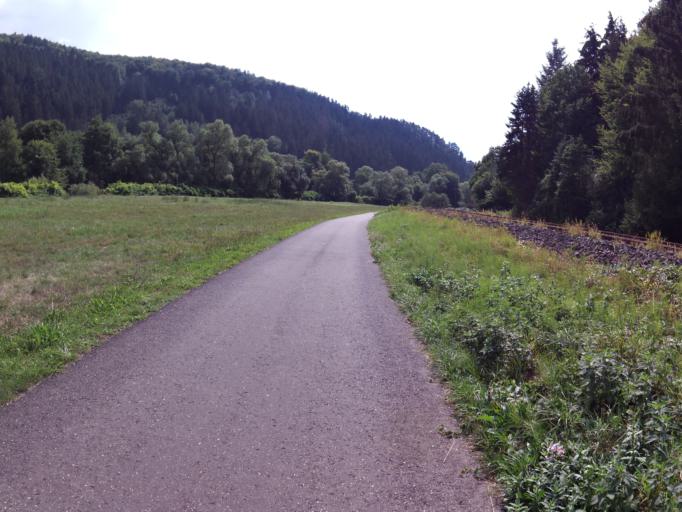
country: DE
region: Rheinland-Pfalz
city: Kordel
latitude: 49.8301
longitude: 6.6501
